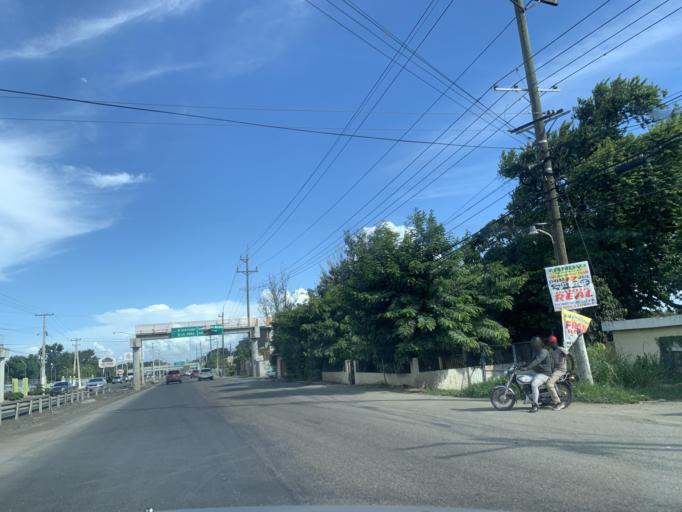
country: DO
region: Santiago
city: Villa Gonzalez
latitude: 19.5201
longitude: -70.7660
